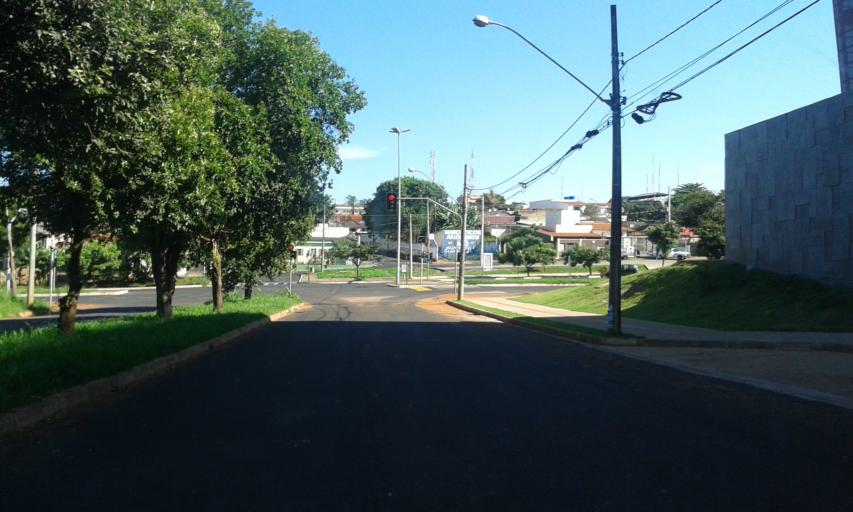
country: BR
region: Minas Gerais
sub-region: Uberlandia
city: Uberlandia
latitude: -18.8967
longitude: -48.2545
